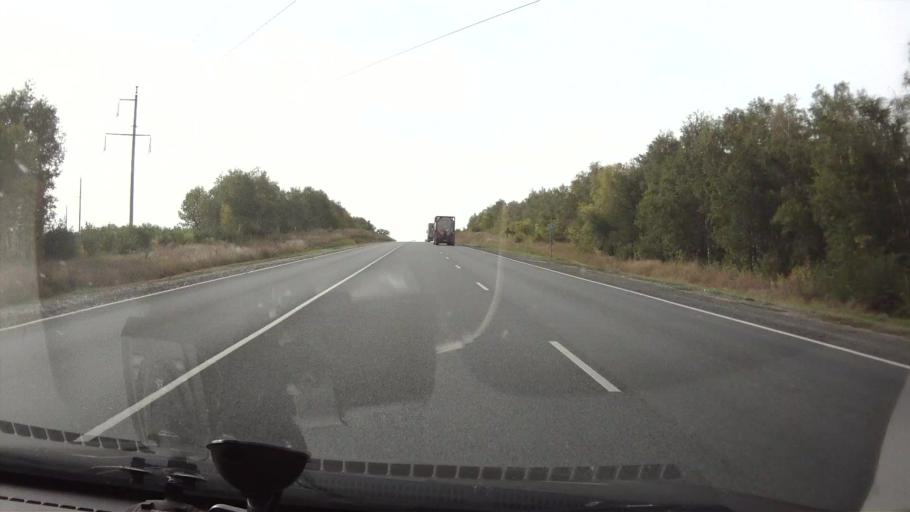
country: RU
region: Saratov
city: Tersa
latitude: 52.1023
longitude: 47.5096
